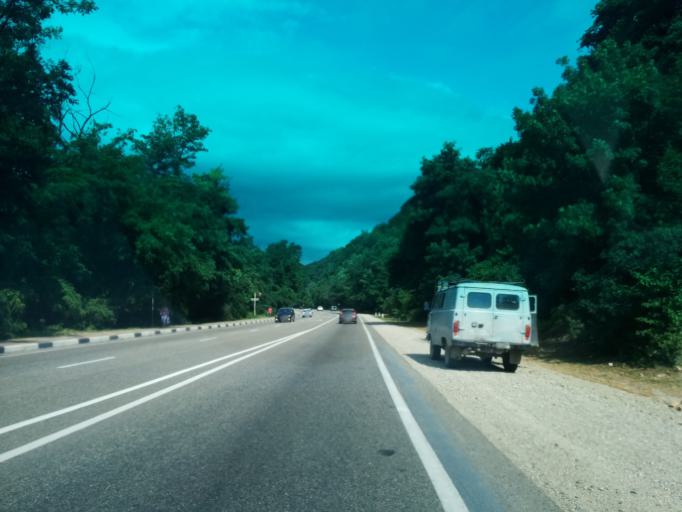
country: RU
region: Krasnodarskiy
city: Nebug
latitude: 44.1677
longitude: 38.9885
